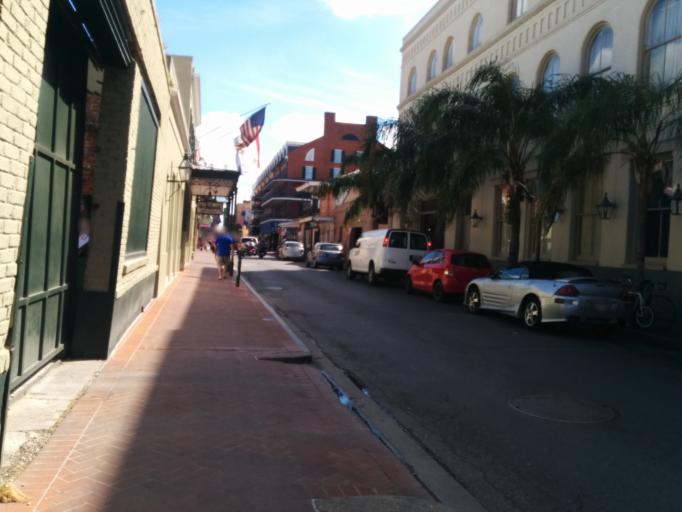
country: US
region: Louisiana
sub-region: Orleans Parish
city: New Orleans
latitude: 29.9568
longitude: -90.0684
